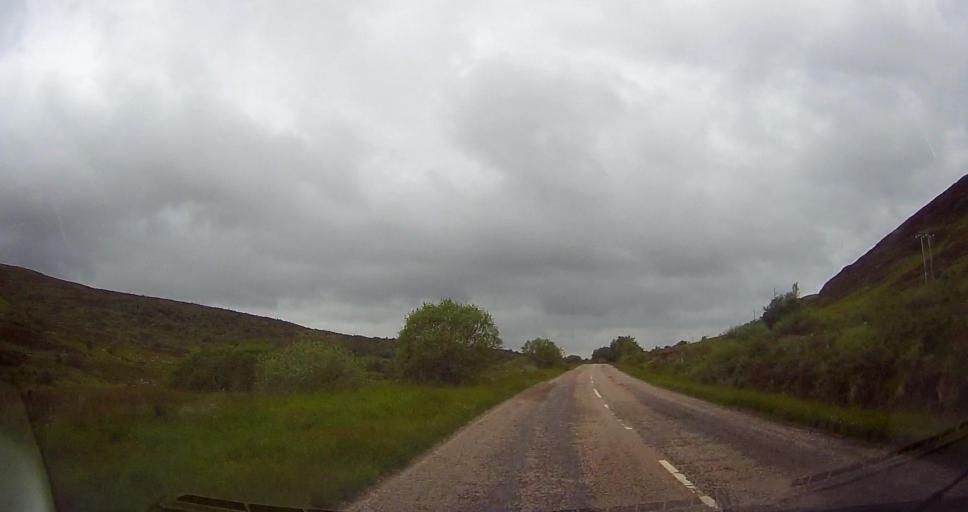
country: GB
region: Scotland
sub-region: Highland
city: Dornoch
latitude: 58.0170
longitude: -4.3180
